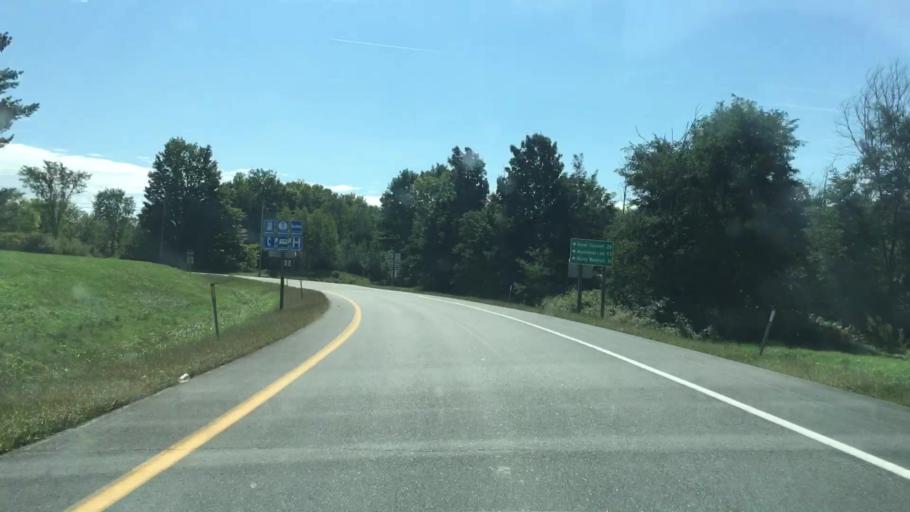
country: US
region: Maine
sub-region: Penobscot County
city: Newport
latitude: 44.8330
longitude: -69.2947
